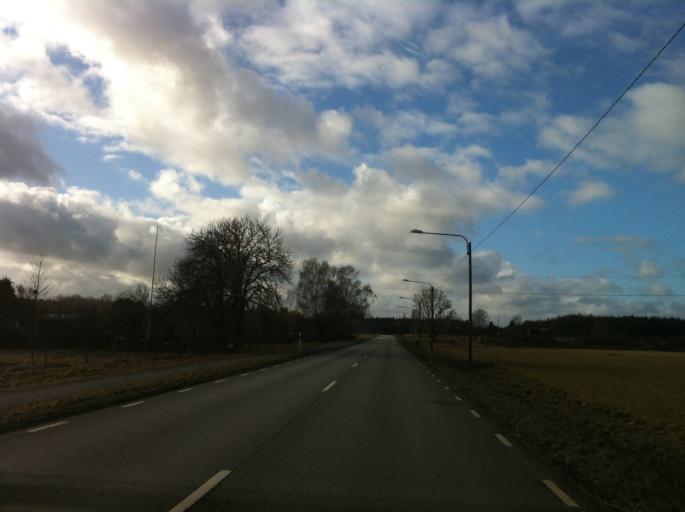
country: SE
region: Blekinge
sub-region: Solvesborgs Kommun
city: Soelvesborg
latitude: 56.0621
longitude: 14.5244
